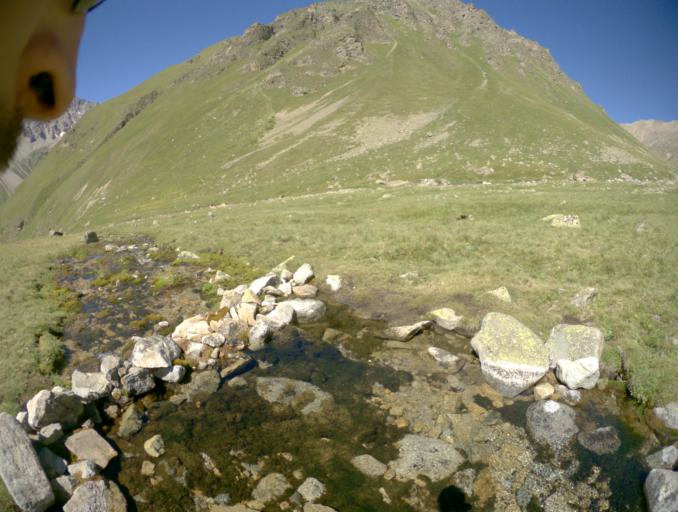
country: RU
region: Kabardino-Balkariya
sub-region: El'brusskiy Rayon
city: El'brus
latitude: 43.3039
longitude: 42.5889
